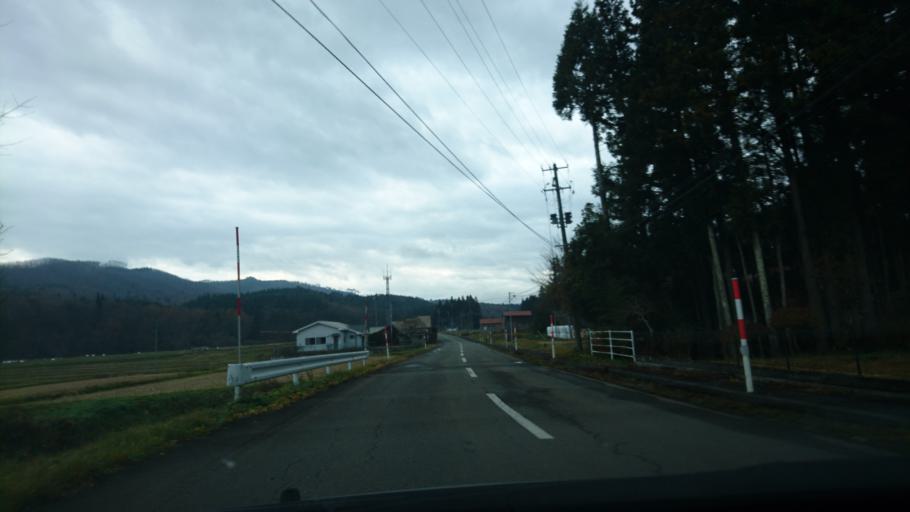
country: JP
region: Iwate
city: Ichinoseki
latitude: 38.9593
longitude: 140.9408
